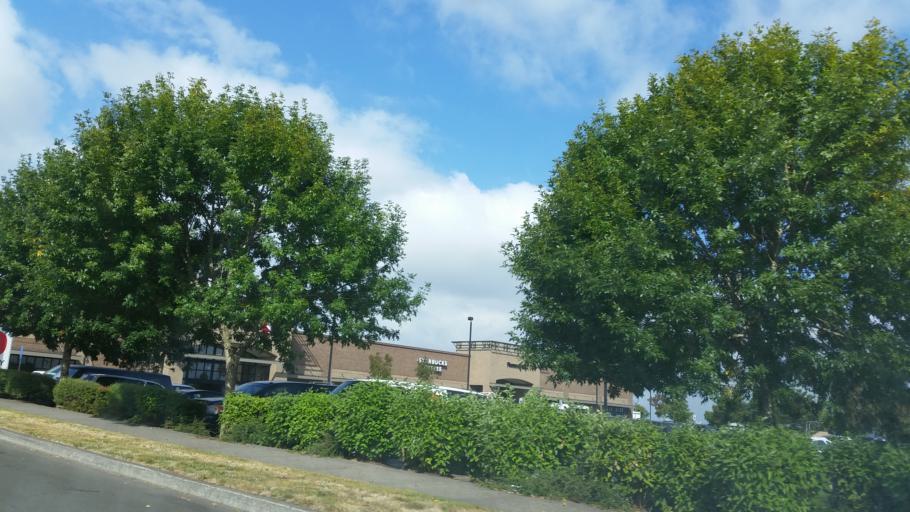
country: US
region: Oregon
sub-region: Clatsop County
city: Astoria
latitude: 46.1923
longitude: -123.8069
